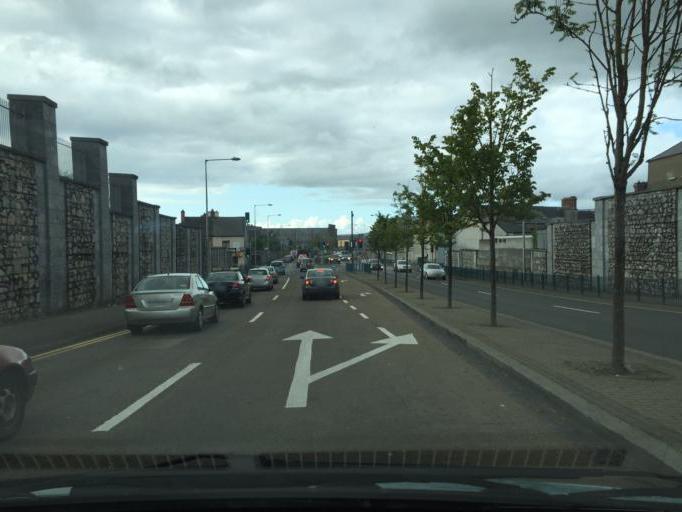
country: IE
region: Connaught
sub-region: Sligo
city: Sligo
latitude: 54.2690
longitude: -8.4802
